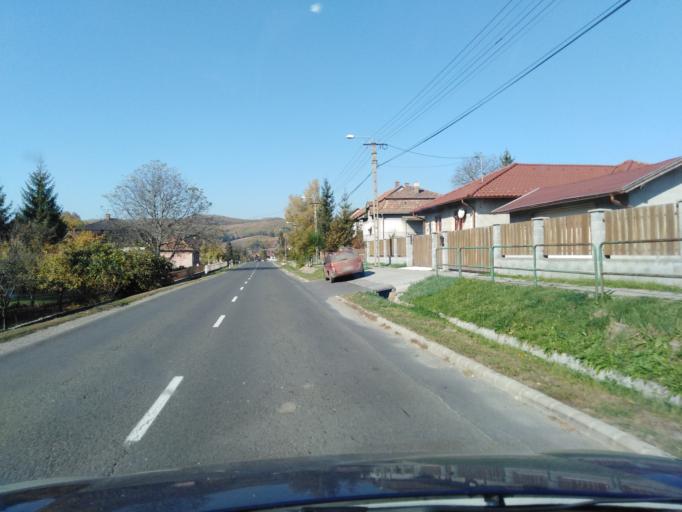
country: HU
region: Nograd
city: Karancslapujto
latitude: 48.1289
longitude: 19.7585
